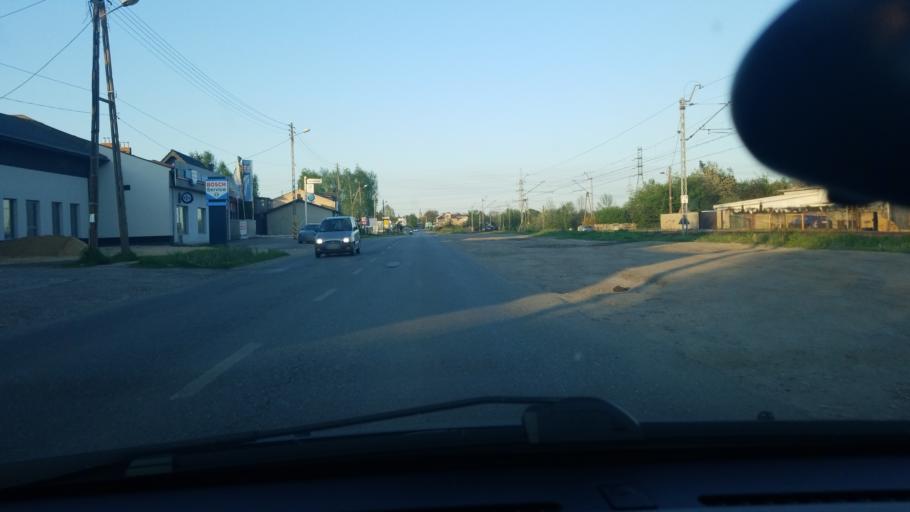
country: PL
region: Silesian Voivodeship
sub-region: Czestochowa
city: Czestochowa
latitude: 50.8007
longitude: 19.0735
